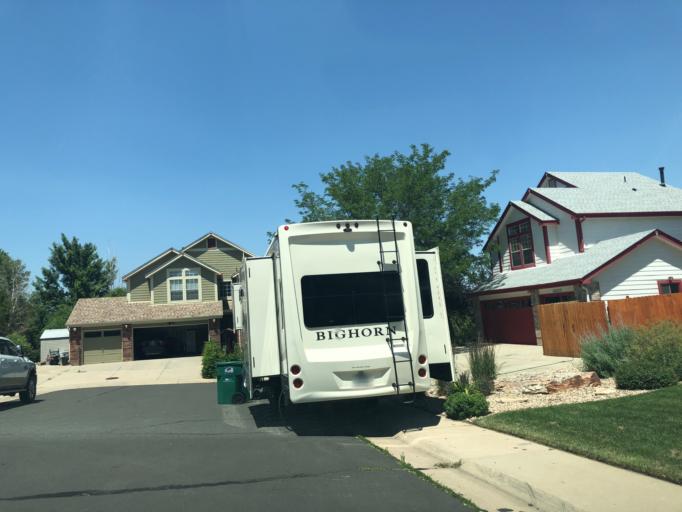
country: US
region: Colorado
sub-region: Arapahoe County
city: Dove Valley
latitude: 39.6288
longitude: -104.7724
